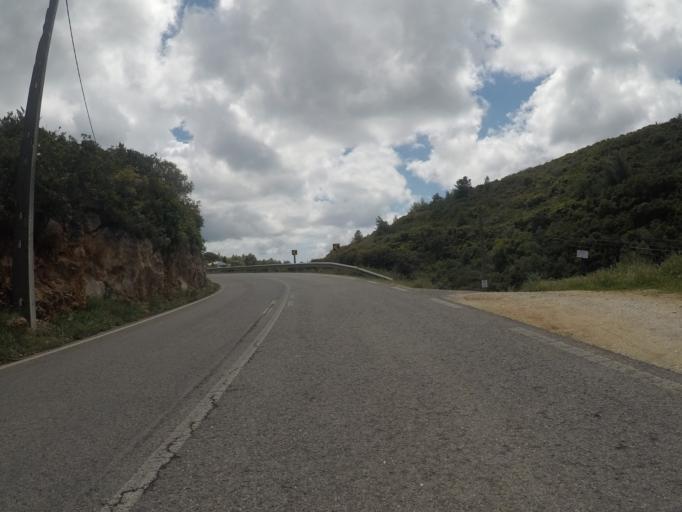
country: PT
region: Faro
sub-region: Vila do Bispo
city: Vila do Bispo
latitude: 37.0700
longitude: -8.8262
